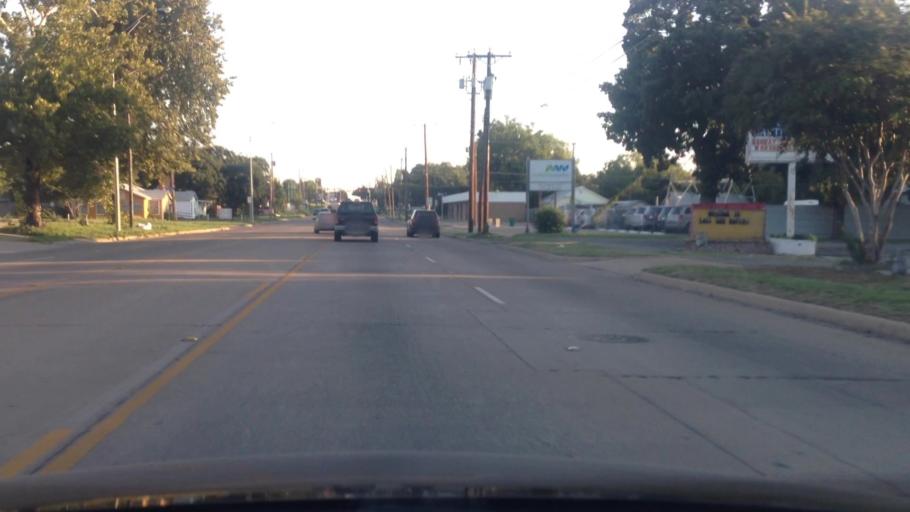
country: US
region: Texas
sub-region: Tarrant County
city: Haltom City
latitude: 32.7905
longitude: -97.2906
